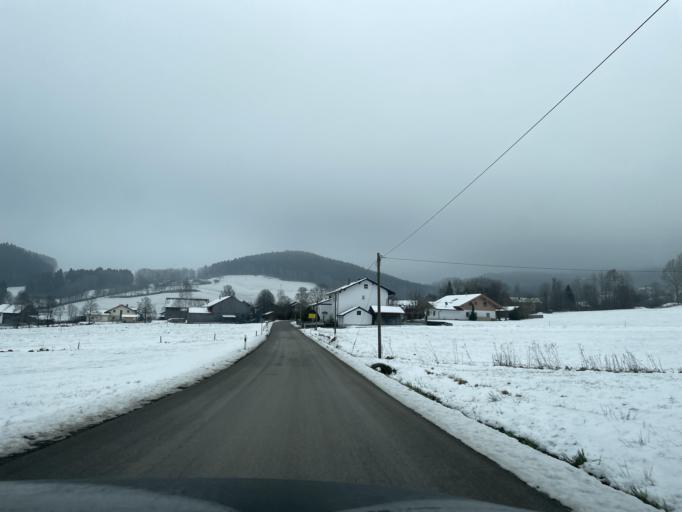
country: DE
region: Bavaria
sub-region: Lower Bavaria
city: Kollnburg
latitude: 49.0156
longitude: 12.8842
